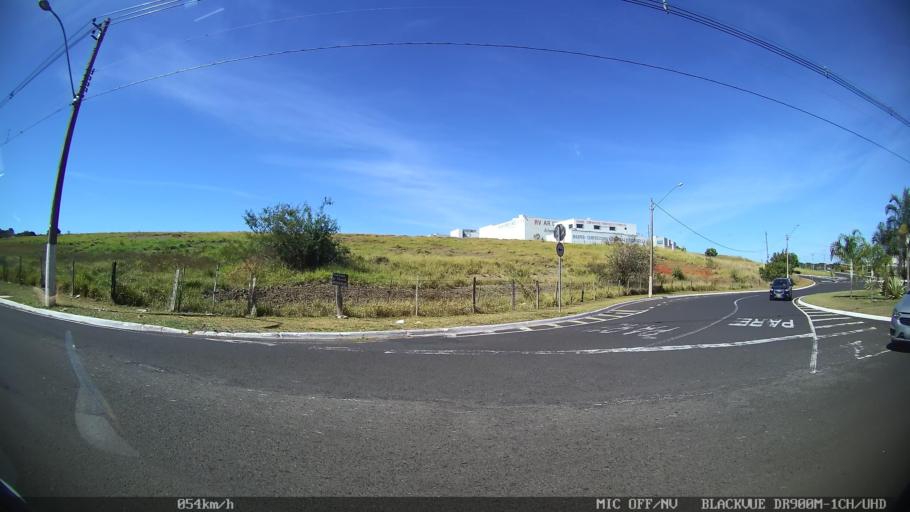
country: BR
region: Sao Paulo
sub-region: Franca
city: Franca
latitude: -20.5323
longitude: -47.3759
